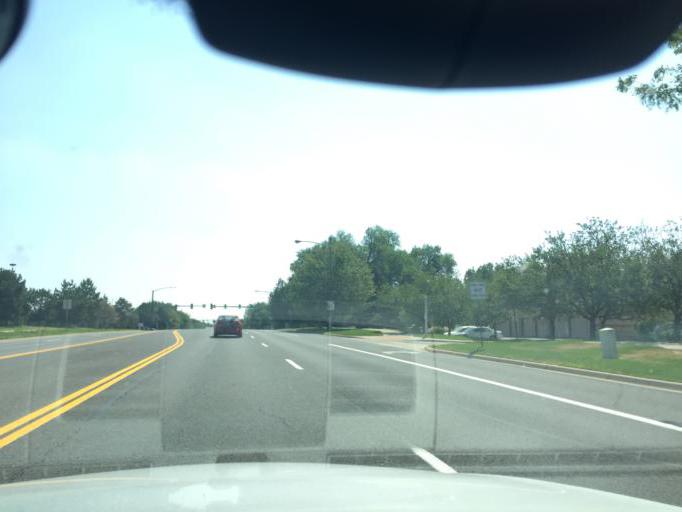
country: US
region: Colorado
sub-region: Adams County
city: Northglenn
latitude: 39.8996
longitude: -105.0362
